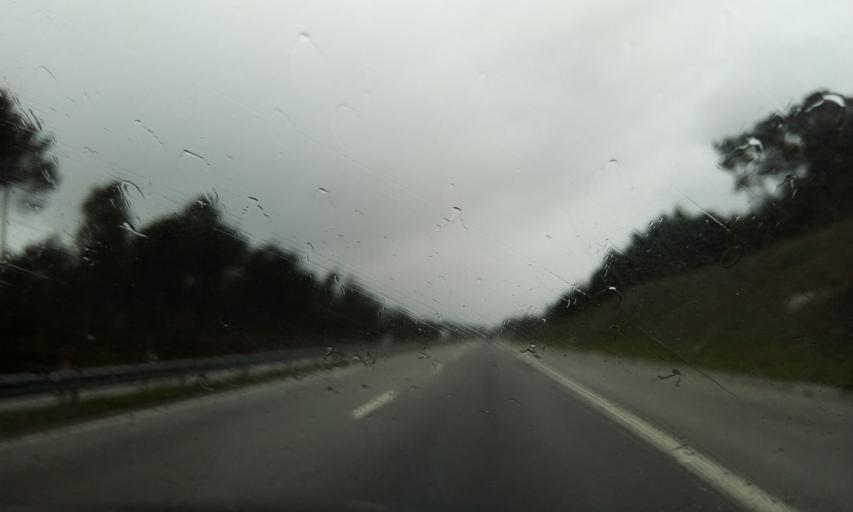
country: PT
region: Guarda
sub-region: Fornos de Algodres
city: Fornos de Algodres
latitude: 40.6143
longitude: -7.6320
